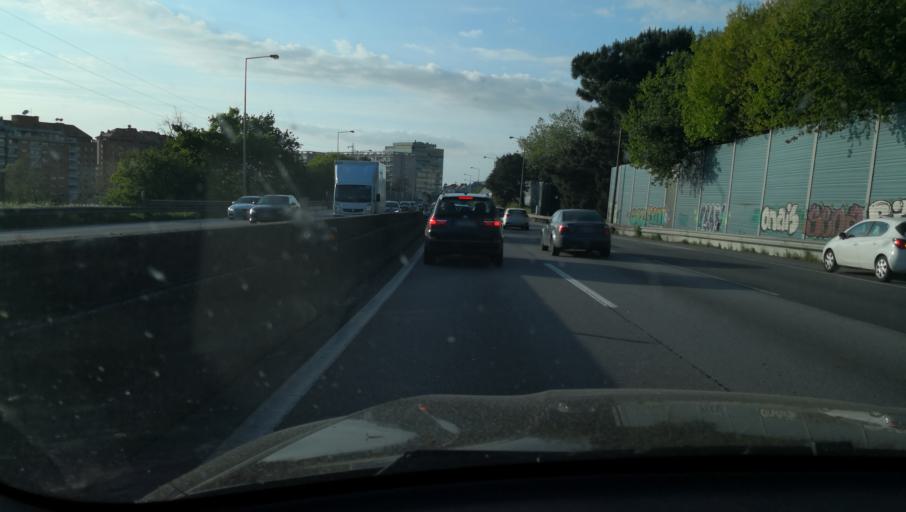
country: PT
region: Porto
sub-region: Vila Nova de Gaia
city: Vila Nova de Gaia
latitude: 41.1381
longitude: -8.6362
